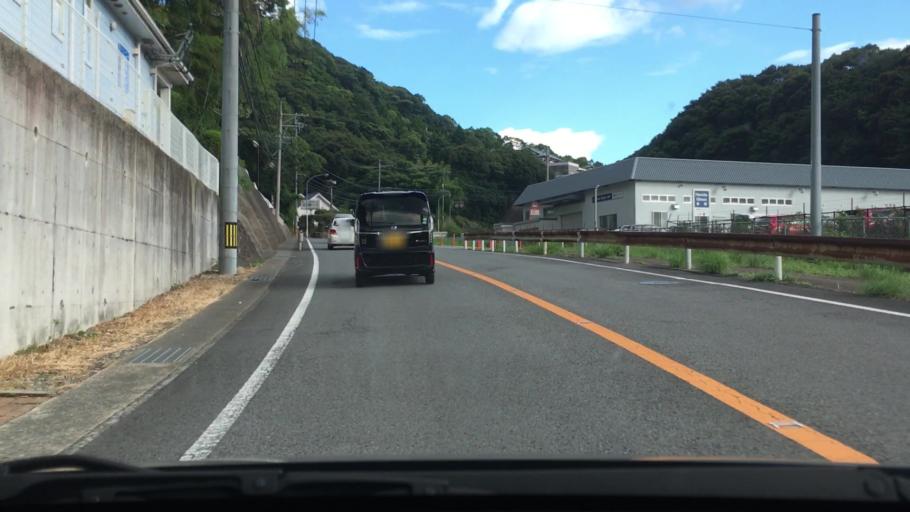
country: JP
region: Nagasaki
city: Togitsu
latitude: 32.8152
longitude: 129.8083
